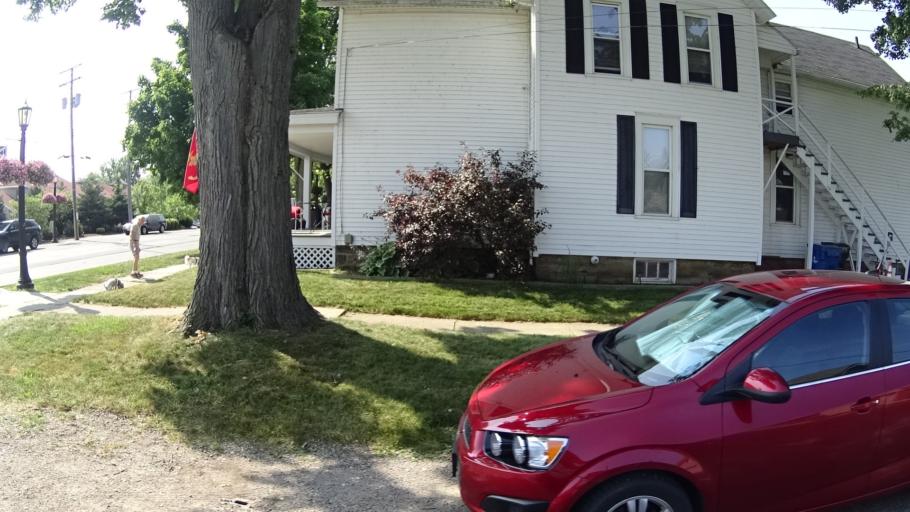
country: US
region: Ohio
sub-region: Lorain County
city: Vermilion
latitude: 41.4233
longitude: -82.3655
